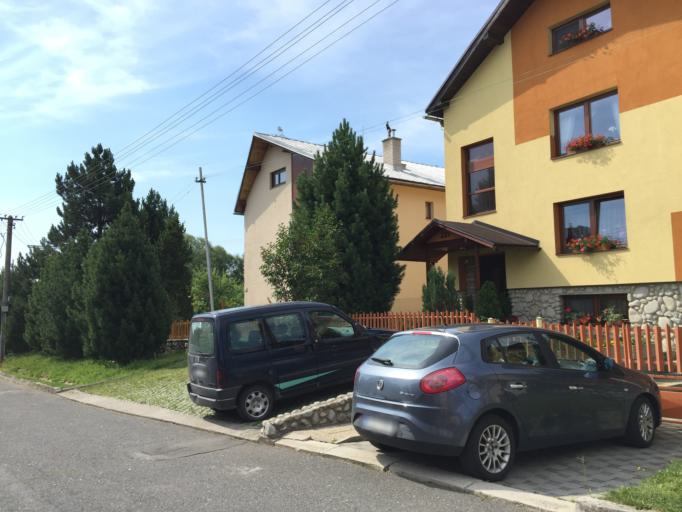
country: SK
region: Presovsky
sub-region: Okres Poprad
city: Nova Lesna
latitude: 49.1232
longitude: 20.2631
